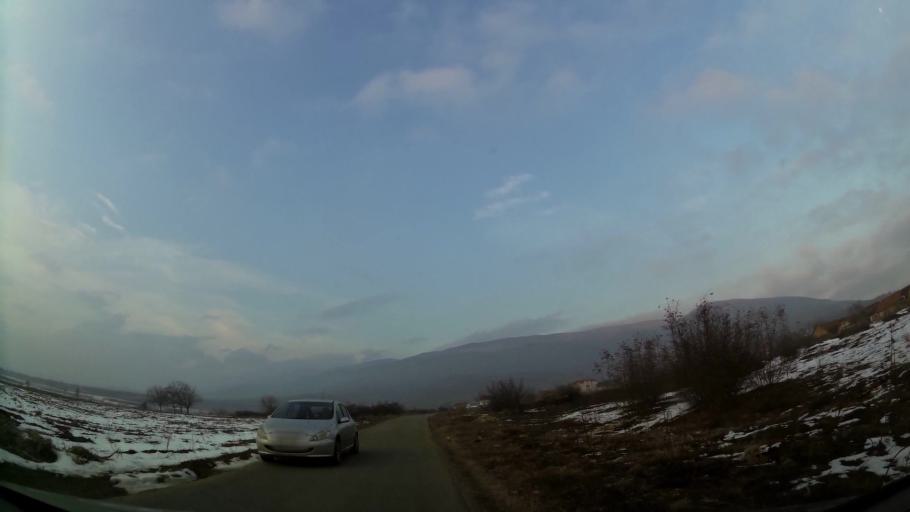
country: MK
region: Aracinovo
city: Arachinovo
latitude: 42.0274
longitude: 21.5453
